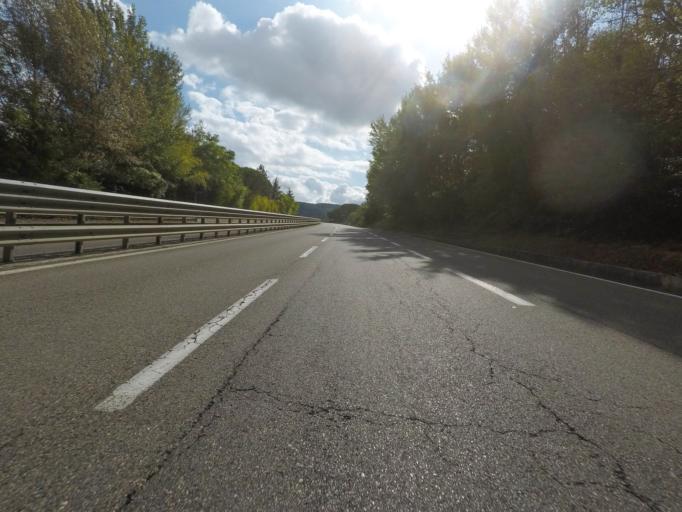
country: IT
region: Tuscany
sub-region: Provincia di Siena
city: Rapolano Terme
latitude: 43.2980
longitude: 11.6010
